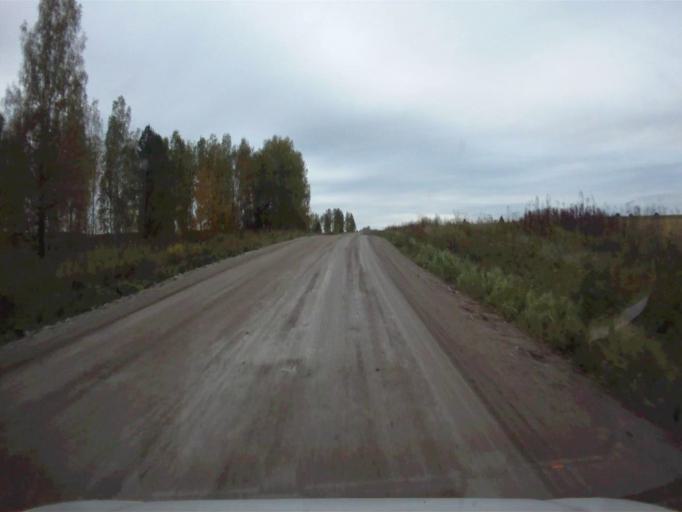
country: RU
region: Sverdlovsk
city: Mikhaylovsk
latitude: 56.1765
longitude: 59.2121
